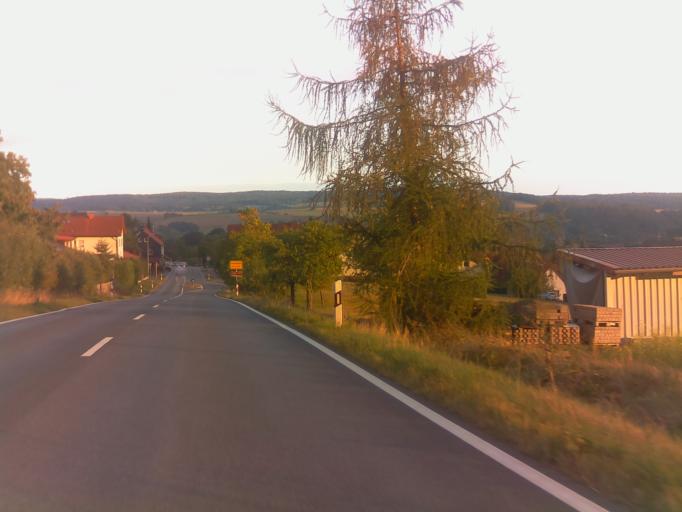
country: DE
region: Bavaria
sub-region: Regierungsbezirk Unterfranken
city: Oberleichtersbach
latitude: 50.2779
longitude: 9.8041
